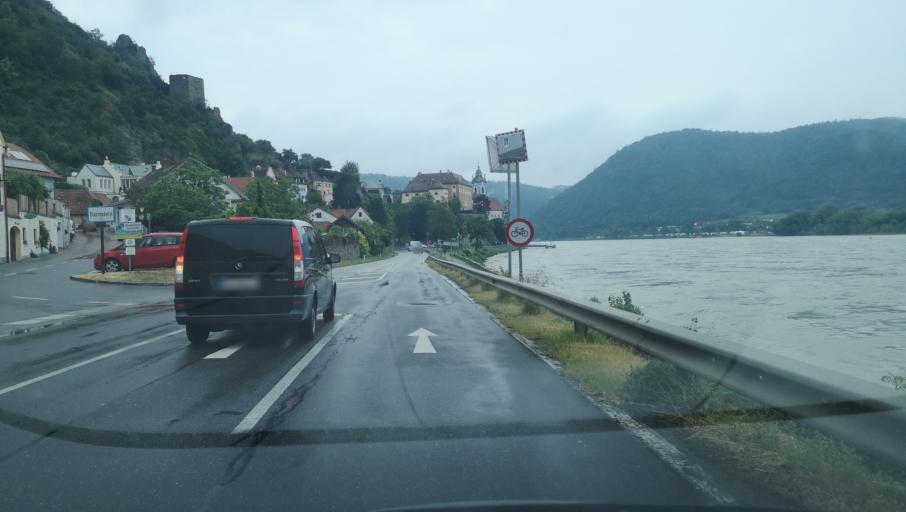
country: AT
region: Lower Austria
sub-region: Politischer Bezirk Krems
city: Durnstein
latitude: 48.3993
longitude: 15.5180
